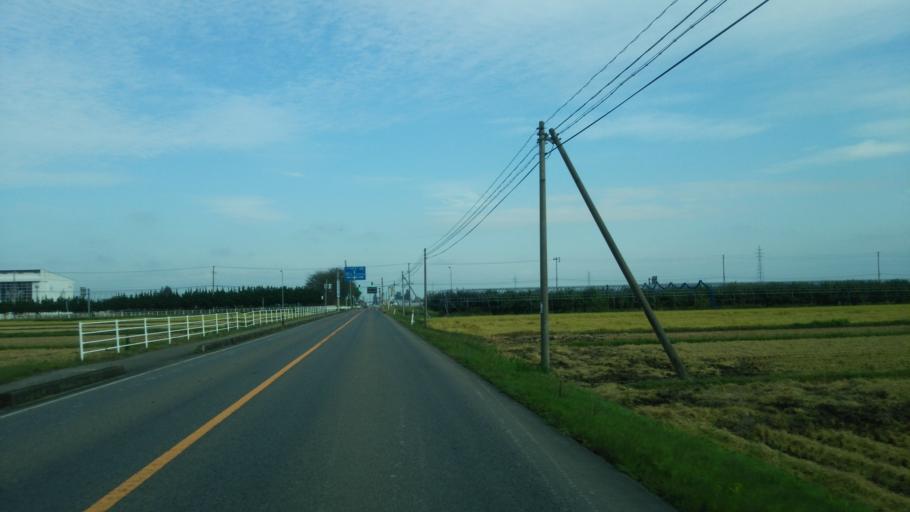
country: JP
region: Fukushima
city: Kitakata
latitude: 37.5057
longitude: 139.8693
